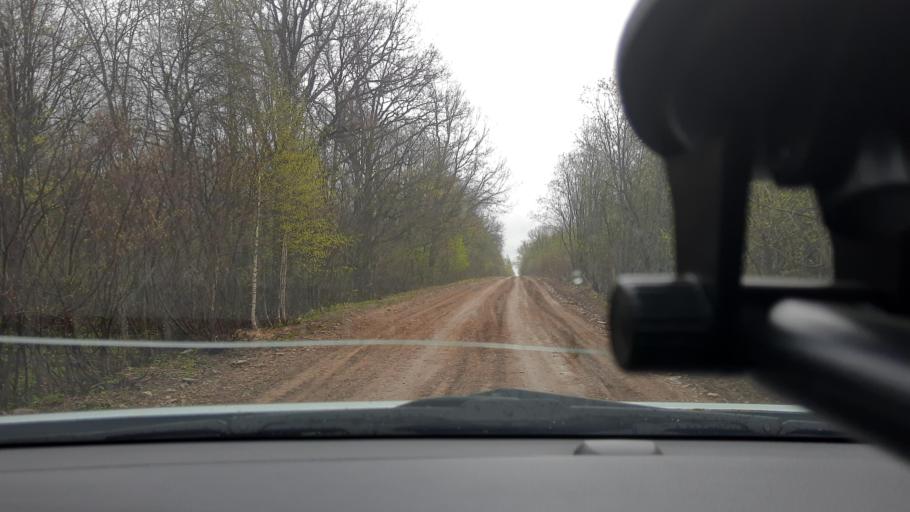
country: RU
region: Bashkortostan
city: Pavlovka
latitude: 55.4308
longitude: 56.3509
